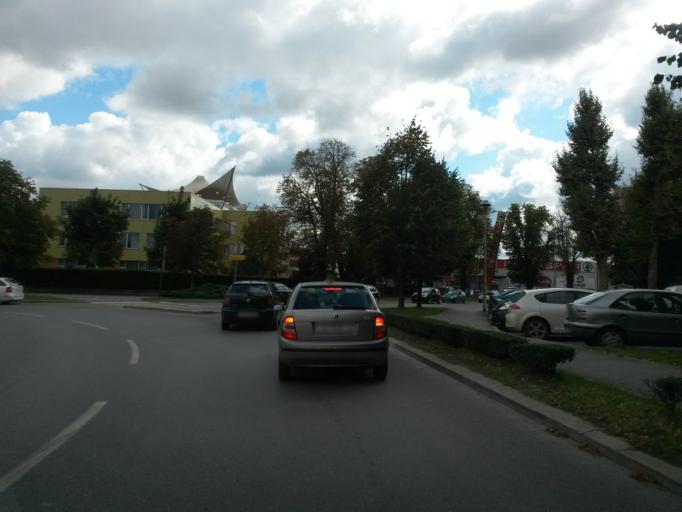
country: HR
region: Osjecko-Baranjska
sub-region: Grad Osijek
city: Osijek
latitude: 45.5544
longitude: 18.6749
